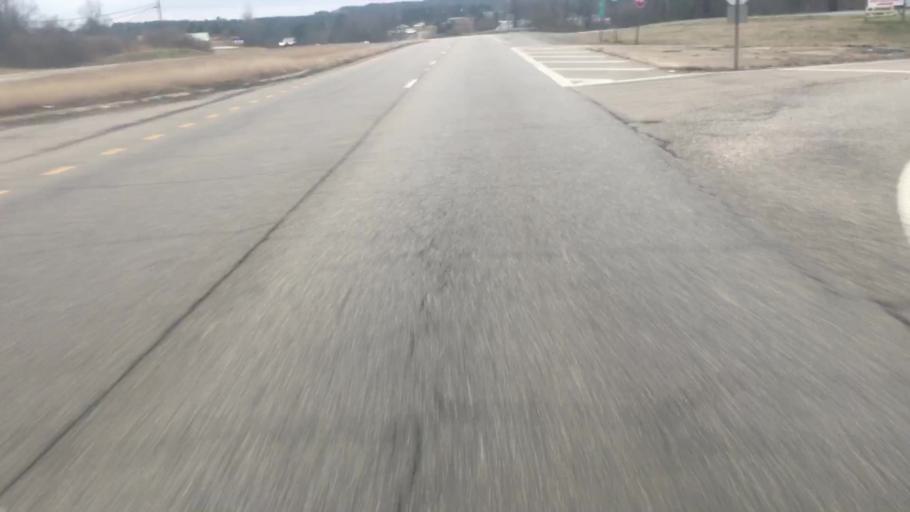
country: US
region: Alabama
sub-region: Walker County
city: Dora
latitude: 33.7969
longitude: -87.1110
